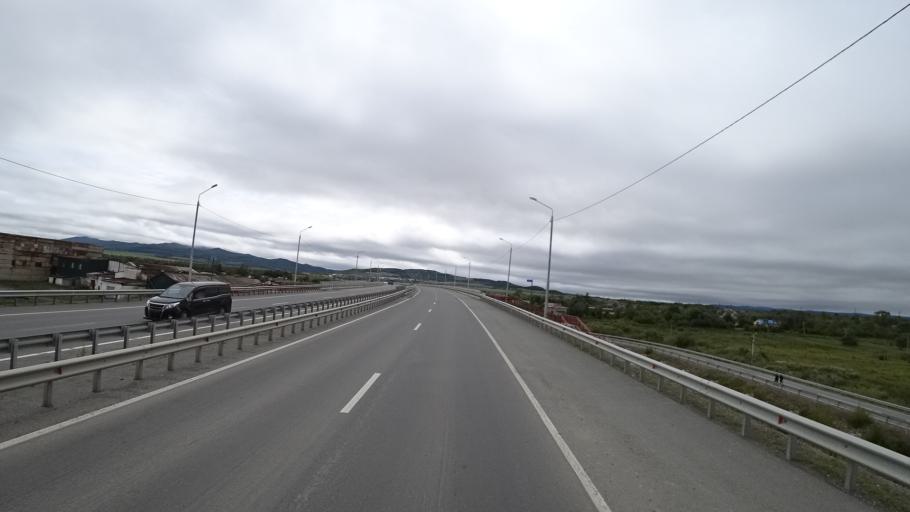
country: RU
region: Primorskiy
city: Monastyrishche
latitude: 44.1937
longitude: 132.4428
